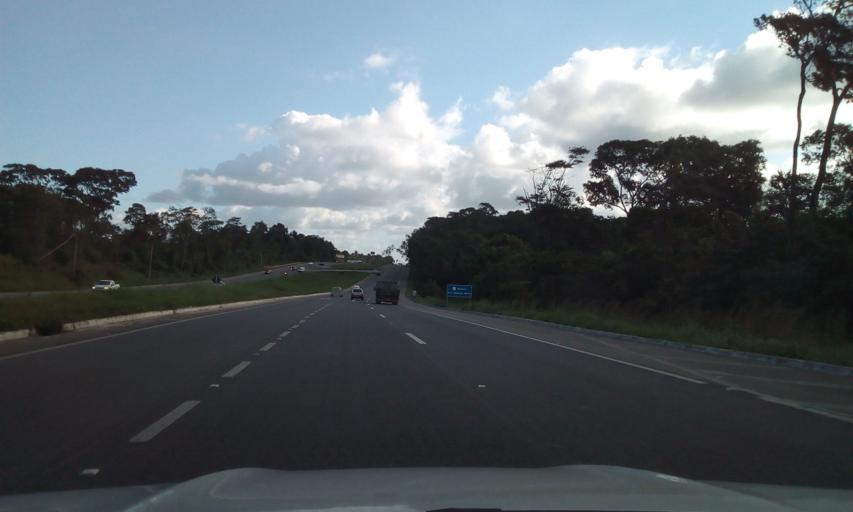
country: BR
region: Paraiba
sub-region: Santa Rita
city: Santa Rita
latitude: -7.1432
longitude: -34.9963
